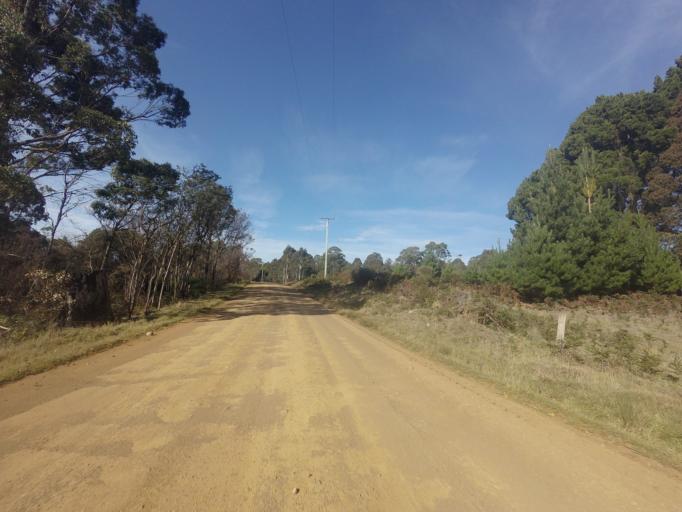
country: AU
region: Tasmania
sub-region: Sorell
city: Sorell
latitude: -42.5053
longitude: 147.5483
